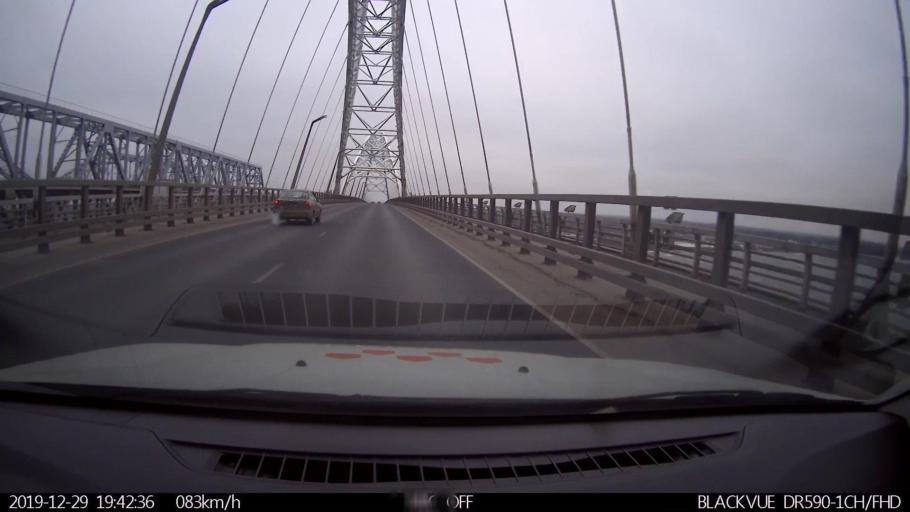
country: RU
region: Nizjnij Novgorod
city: Neklyudovo
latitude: 56.3530
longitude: 43.9248
